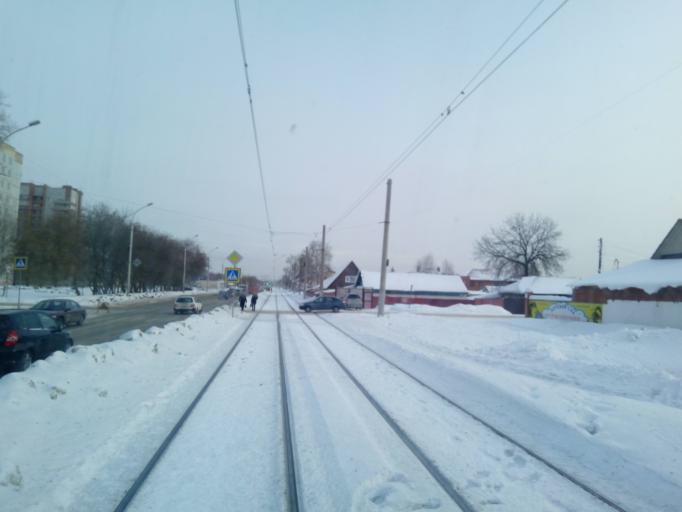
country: RU
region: Novosibirsk
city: Tolmachevo
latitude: 54.9800
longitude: 82.8306
